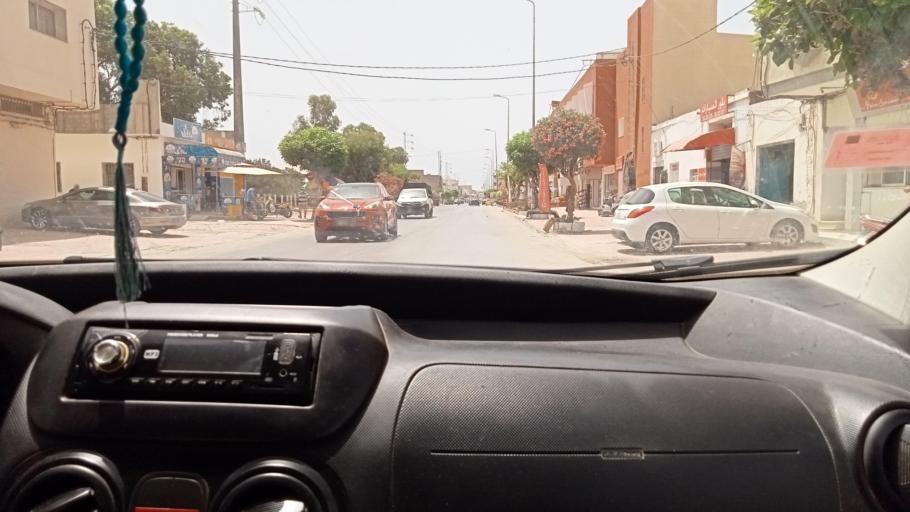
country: TN
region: Nabul
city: Qulaybiyah
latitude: 36.8587
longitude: 11.0906
